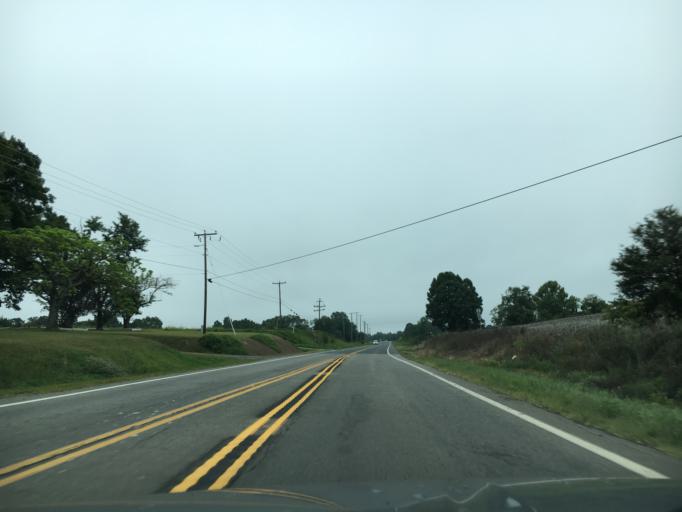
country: US
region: Virginia
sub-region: Campbell County
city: Brookneal
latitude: 37.0850
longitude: -78.9873
